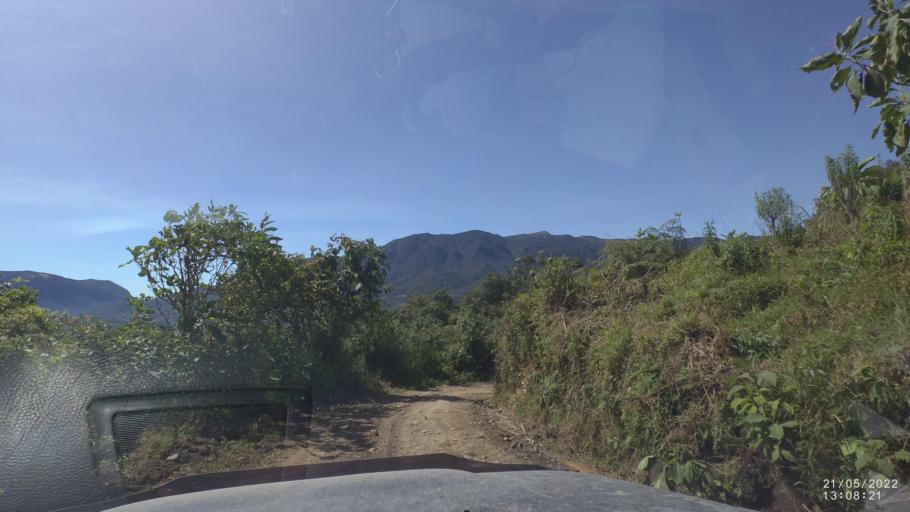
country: BO
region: Cochabamba
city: Colomi
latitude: -17.1478
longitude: -65.9430
